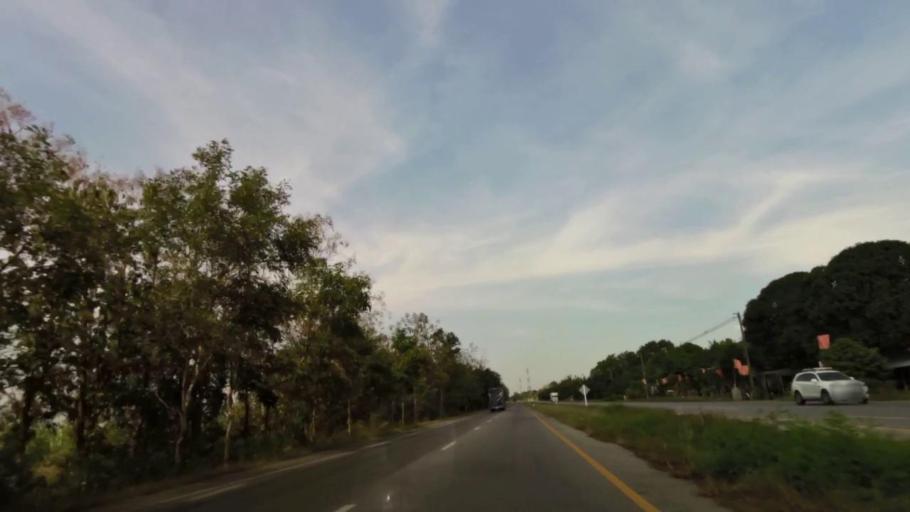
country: TH
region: Uttaradit
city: Tron
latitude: 17.5257
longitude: 100.2145
